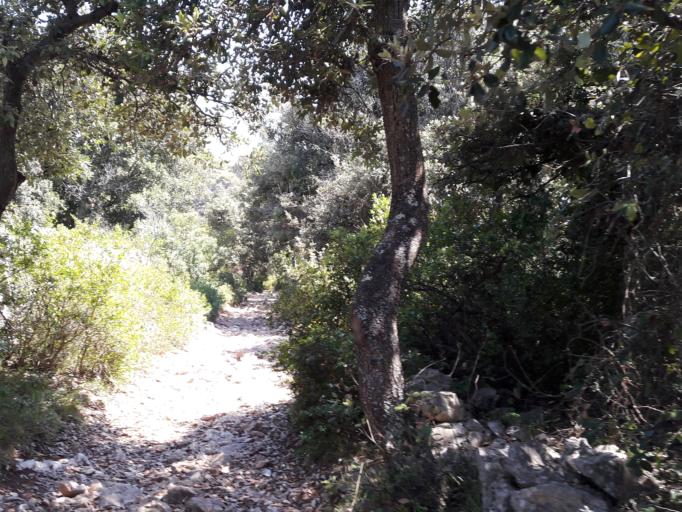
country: HR
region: Licko-Senjska
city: Novalja
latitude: 44.3605
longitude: 14.7018
